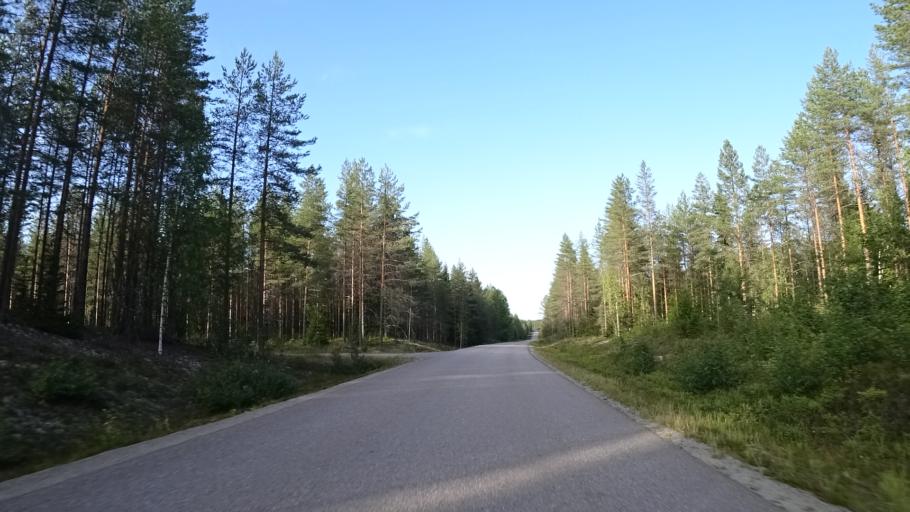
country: FI
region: North Karelia
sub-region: Joensuu
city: Eno
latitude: 63.0600
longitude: 30.5433
